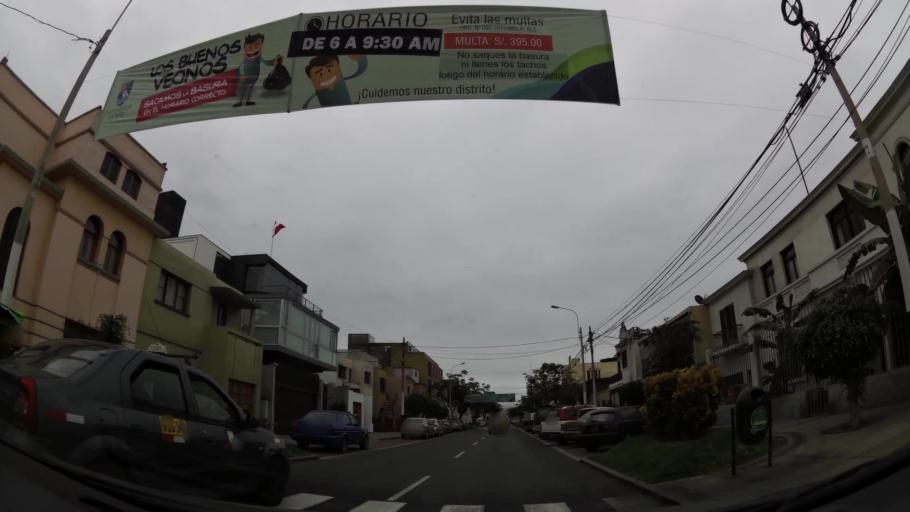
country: PE
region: Callao
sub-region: Callao
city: Callao
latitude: -12.0698
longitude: -77.1615
